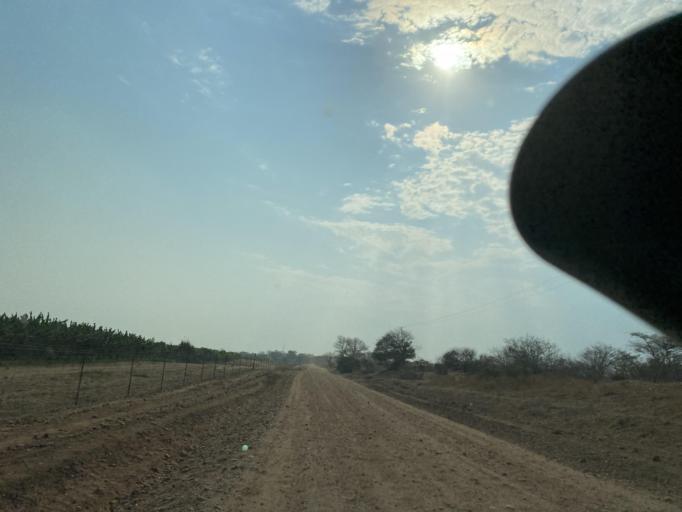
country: ZW
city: Chirundu
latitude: -15.9309
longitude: 28.9583
